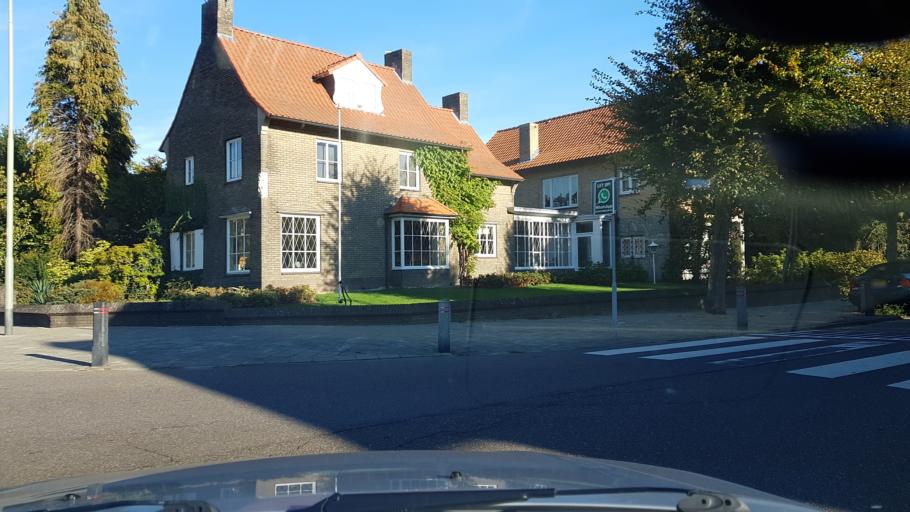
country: NL
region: Limburg
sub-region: Gemeente Schinnen
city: Puth
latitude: 50.9688
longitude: 5.8339
